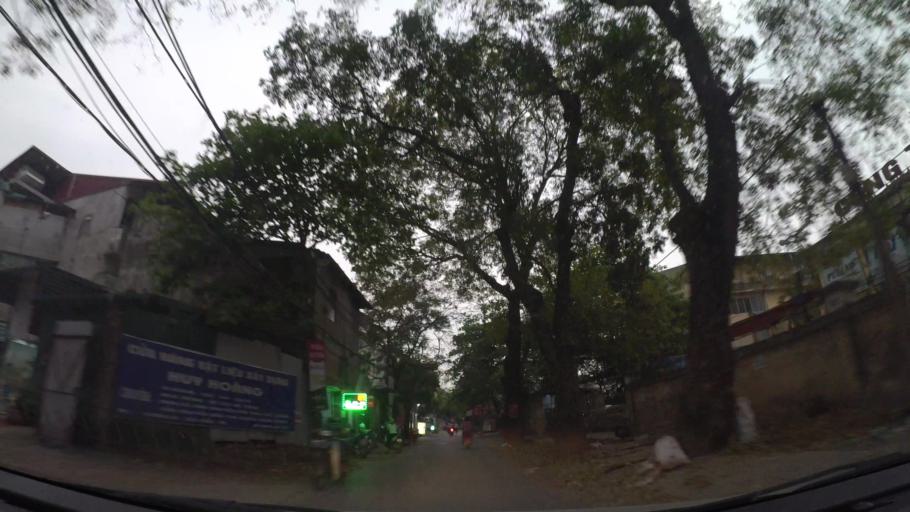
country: VN
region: Ha Noi
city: Cau Dien
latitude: 21.0391
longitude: 105.7607
